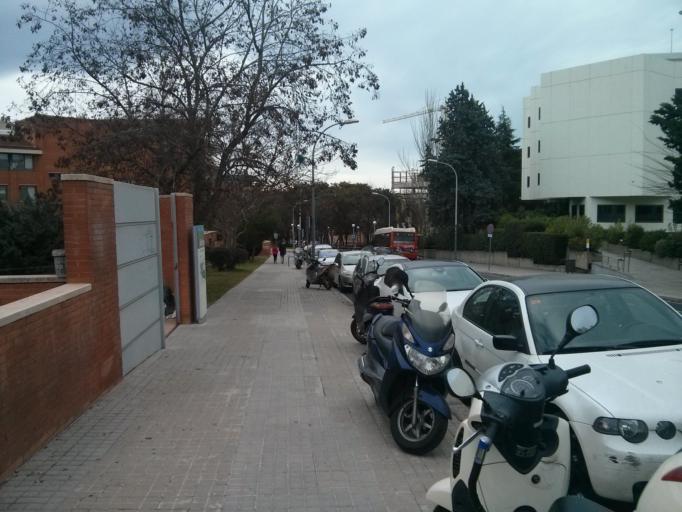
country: ES
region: Catalonia
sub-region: Provincia de Barcelona
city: les Corts
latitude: 41.3902
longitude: 2.1133
